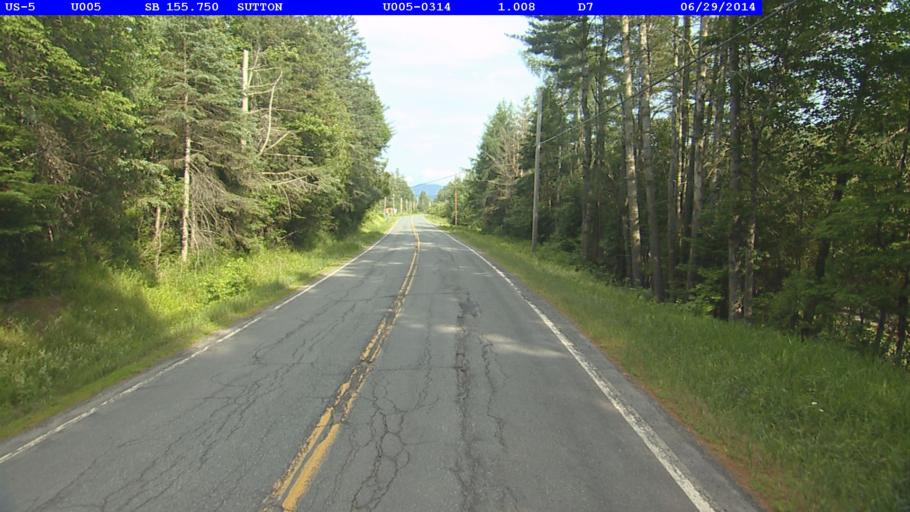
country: US
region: Vermont
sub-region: Caledonia County
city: Lyndonville
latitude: 44.6466
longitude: -72.0033
